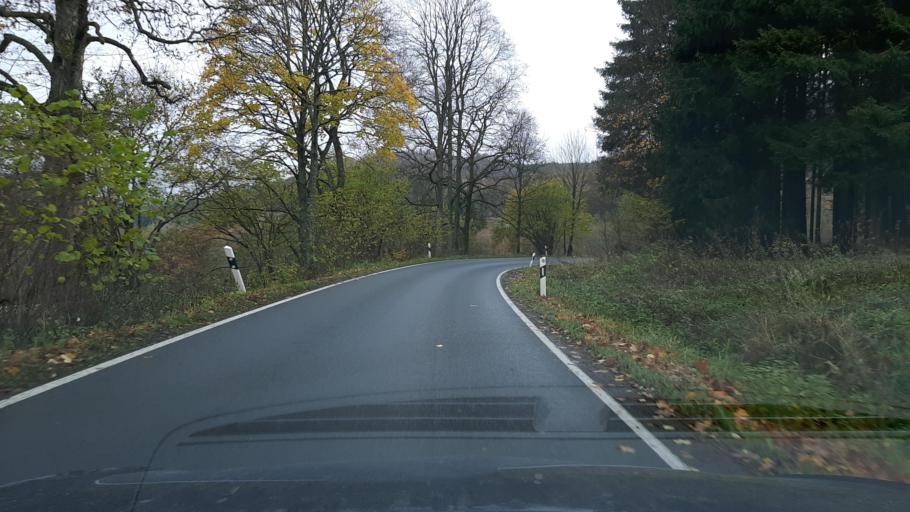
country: DE
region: North Rhine-Westphalia
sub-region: Regierungsbezirk Arnsberg
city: Winterberg
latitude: 51.2162
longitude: 8.4554
